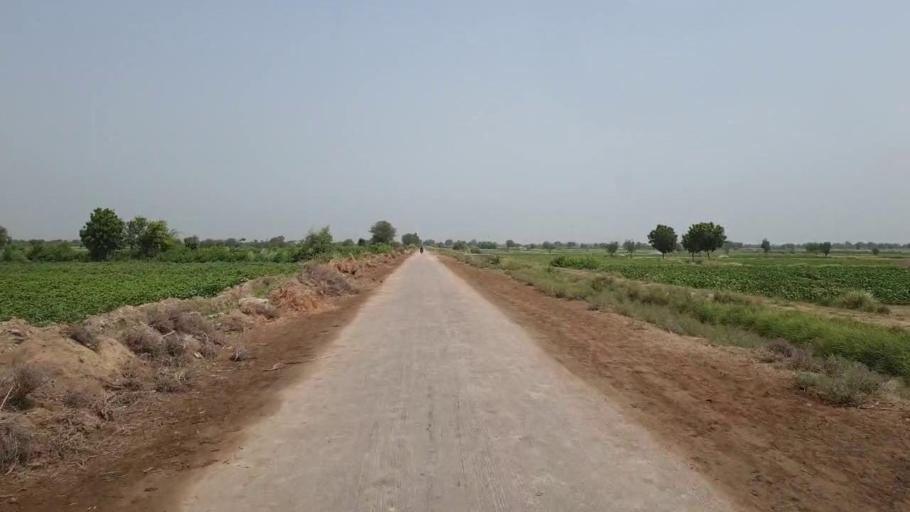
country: PK
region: Sindh
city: Nawabshah
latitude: 26.2719
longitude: 68.3151
